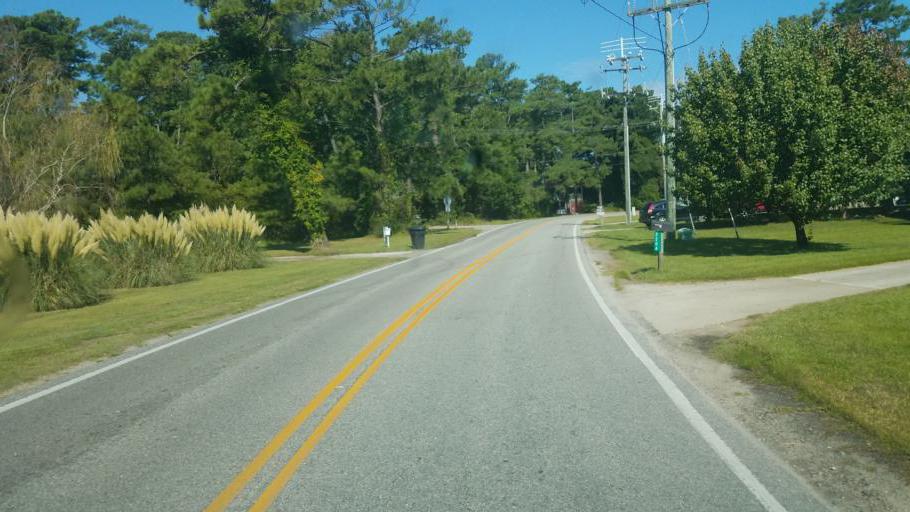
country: US
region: North Carolina
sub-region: Dare County
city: Kill Devil Hills
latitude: 36.0117
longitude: -75.7108
